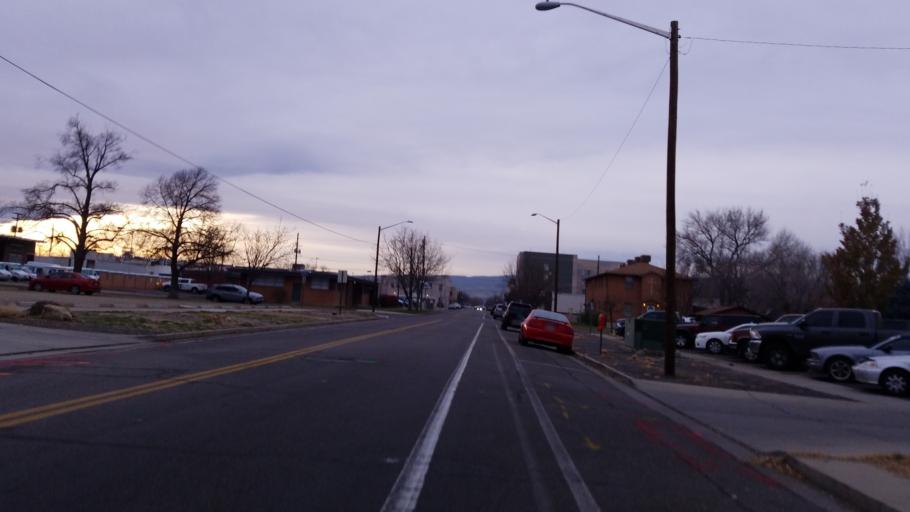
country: US
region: Colorado
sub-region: Mesa County
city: Grand Junction
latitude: 39.0700
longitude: -108.5679
